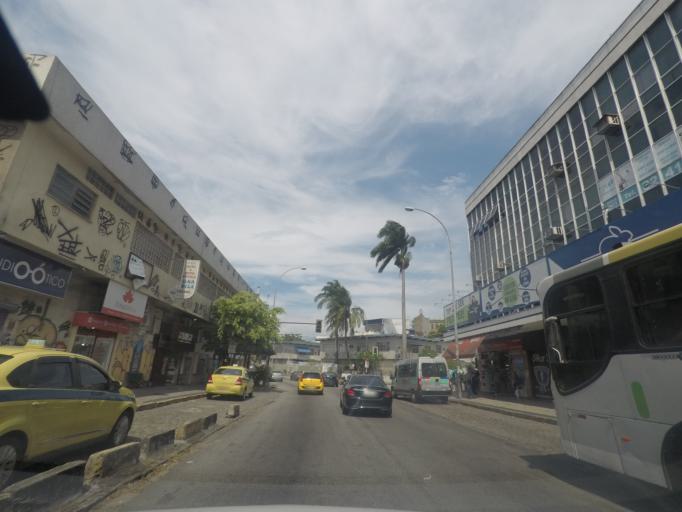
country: BR
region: Rio de Janeiro
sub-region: Rio De Janeiro
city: Rio de Janeiro
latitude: -22.8049
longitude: -43.2068
